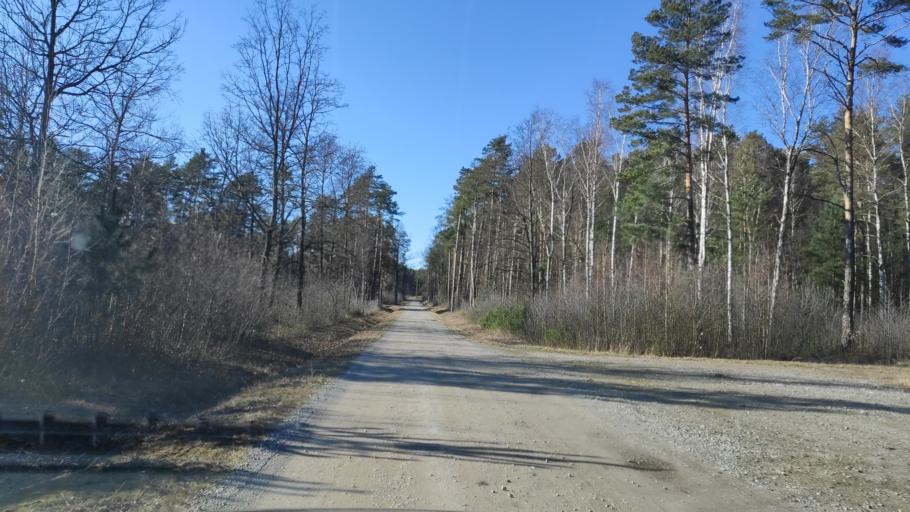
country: PL
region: Masovian Voivodeship
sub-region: Powiat radomski
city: Jedlnia-Letnisko
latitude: 51.4714
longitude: 21.3023
